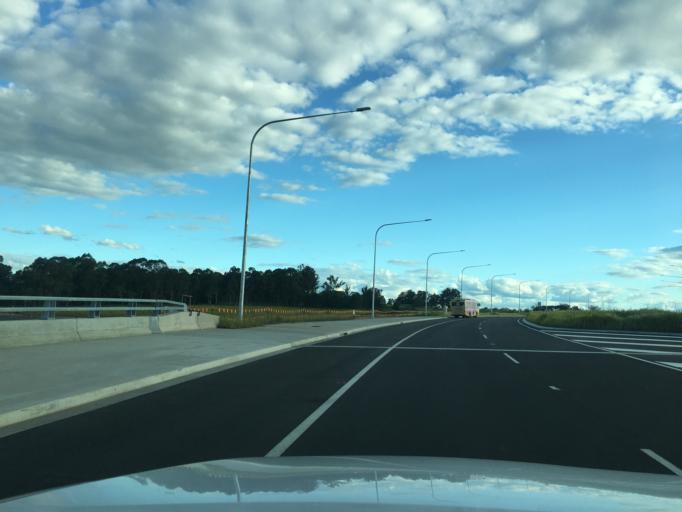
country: AU
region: New South Wales
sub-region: Liverpool
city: Bringelly
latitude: -33.8758
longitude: 150.7497
